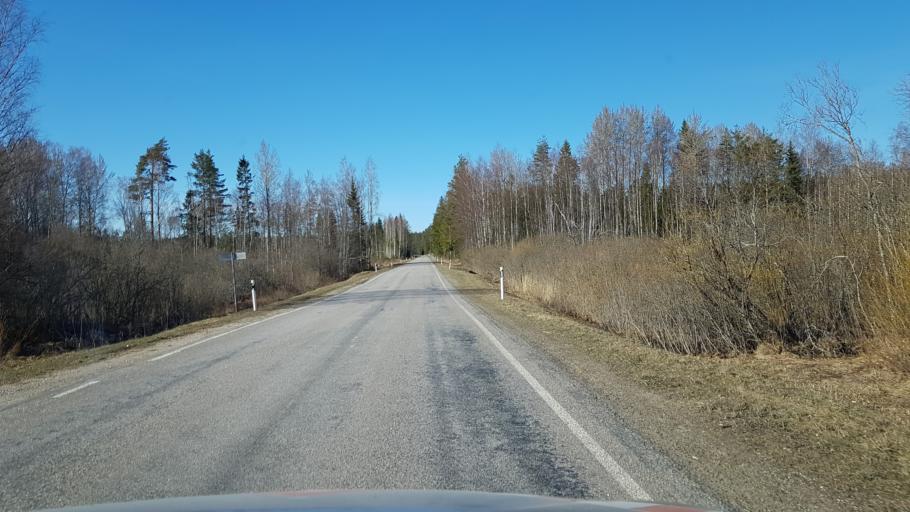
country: EE
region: Laeaene-Virumaa
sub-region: Vinni vald
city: Vinni
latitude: 59.2482
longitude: 26.6886
